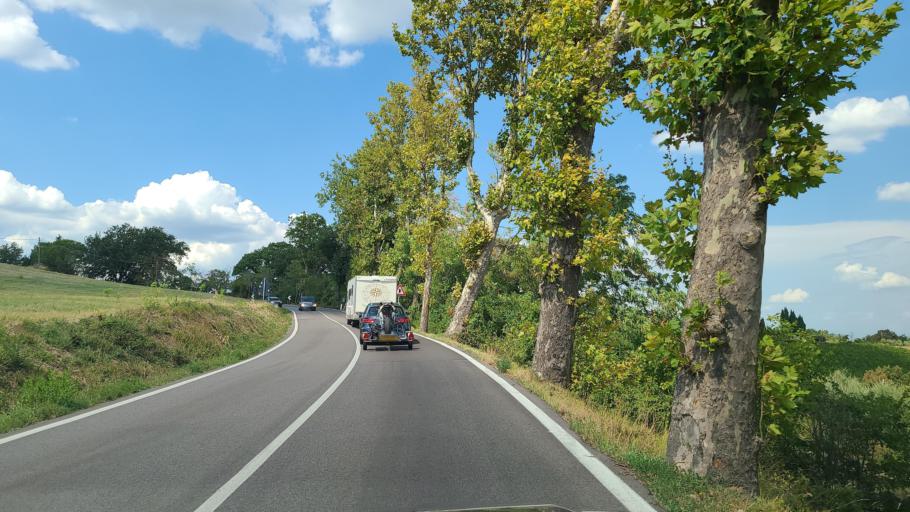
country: IT
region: Tuscany
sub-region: Provincia di Siena
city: Casole d'Elsa
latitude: 43.4039
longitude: 11.0244
